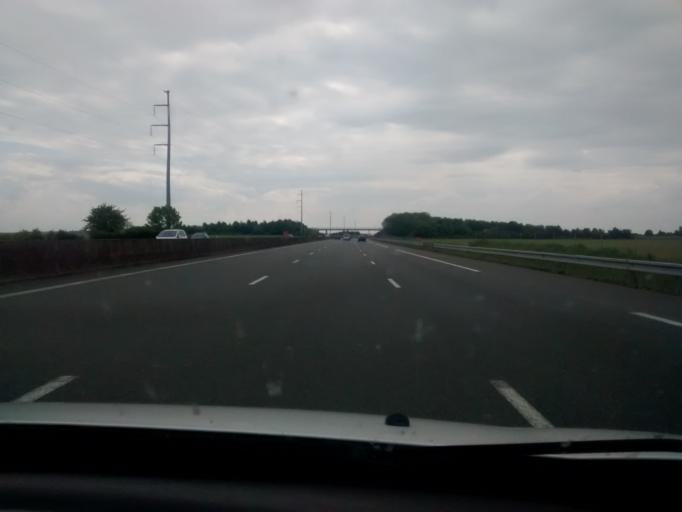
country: FR
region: Centre
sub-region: Departement d'Eure-et-Loir
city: Bailleau-le-Pin
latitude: 48.3354
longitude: 1.3959
